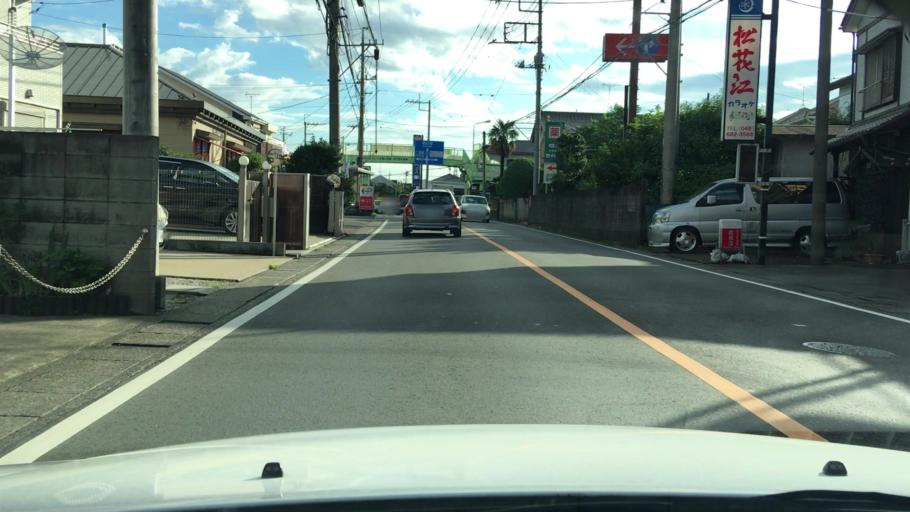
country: JP
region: Saitama
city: Iwatsuki
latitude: 35.9318
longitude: 139.6689
